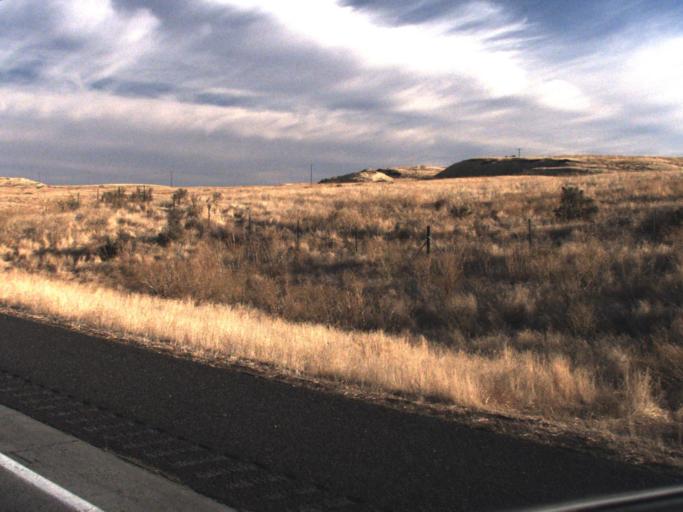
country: US
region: Washington
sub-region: Franklin County
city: Basin City
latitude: 46.4922
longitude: -119.0136
